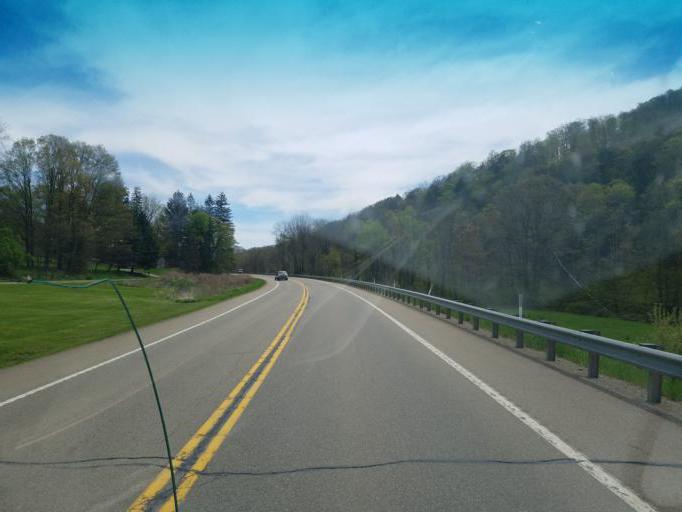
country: US
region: Pennsylvania
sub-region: Potter County
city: Galeton
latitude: 41.7390
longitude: -77.6231
